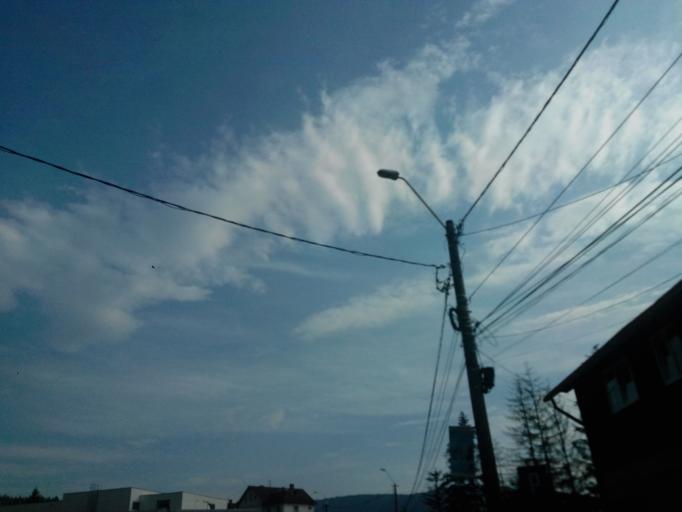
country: RO
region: Prahova
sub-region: Oras Busteni
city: Busteni
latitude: 45.4083
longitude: 25.5352
